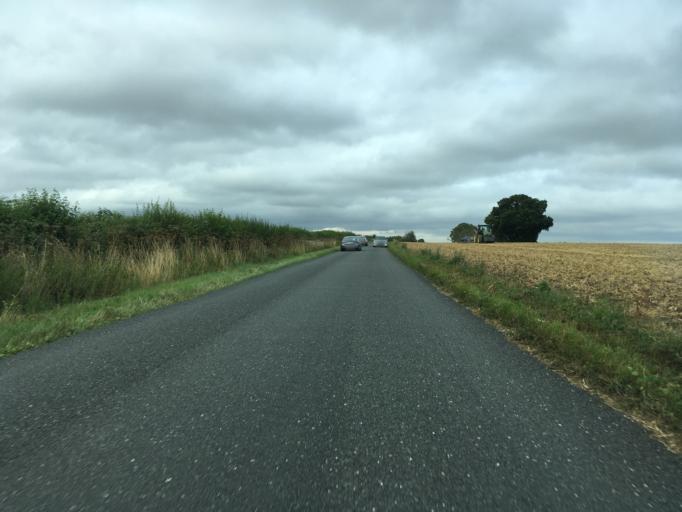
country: GB
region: England
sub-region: Hampshire
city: Bishops Waltham
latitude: 51.0300
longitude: -1.2167
